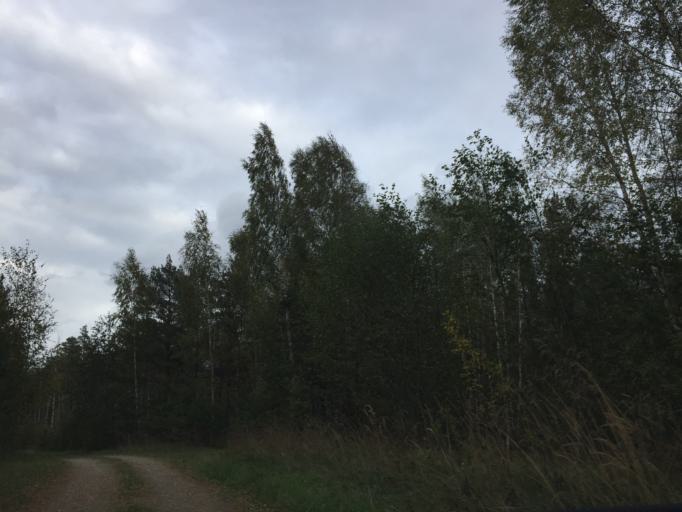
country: LV
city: Tireli
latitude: 56.8962
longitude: 23.5199
